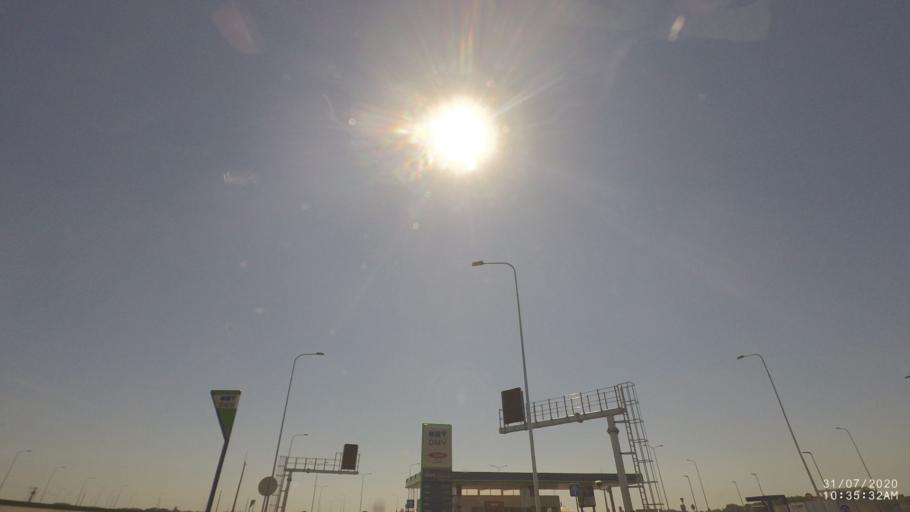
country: SK
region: Trnavsky
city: Samorin
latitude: 48.0119
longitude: 17.4551
